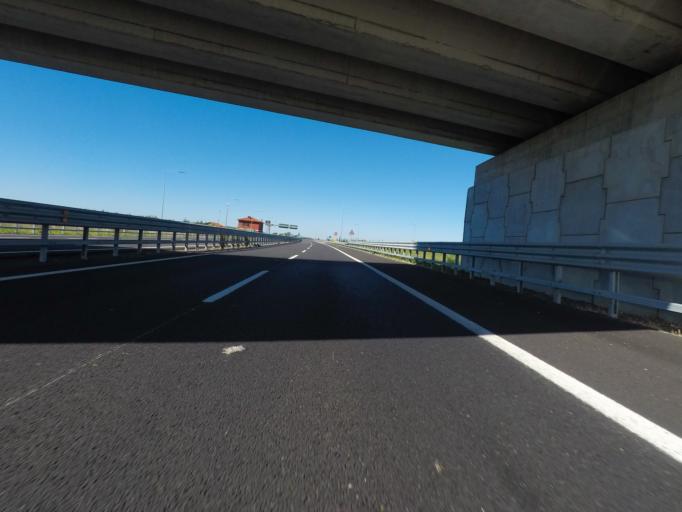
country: IT
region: Latium
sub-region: Provincia di Viterbo
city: Tarquinia
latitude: 42.2116
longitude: 11.7803
